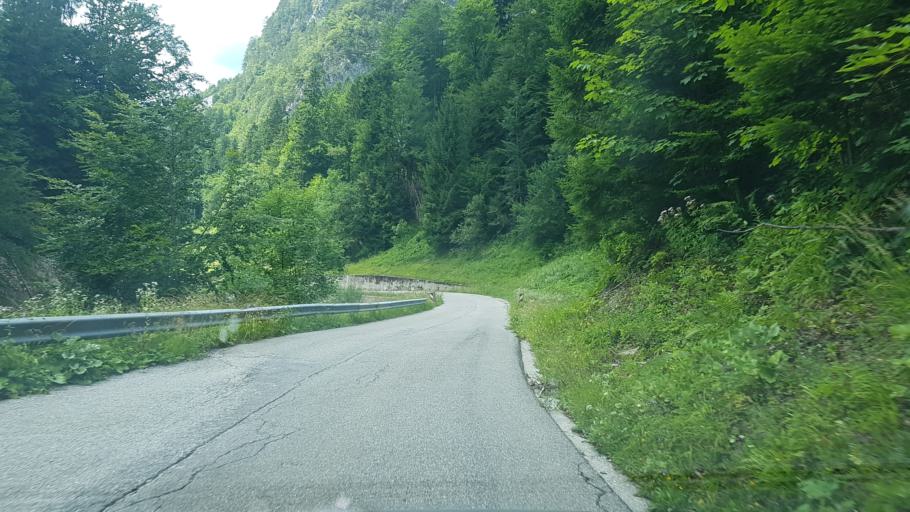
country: IT
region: Friuli Venezia Giulia
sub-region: Provincia di Udine
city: Pontebba
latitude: 46.4994
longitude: 13.2337
